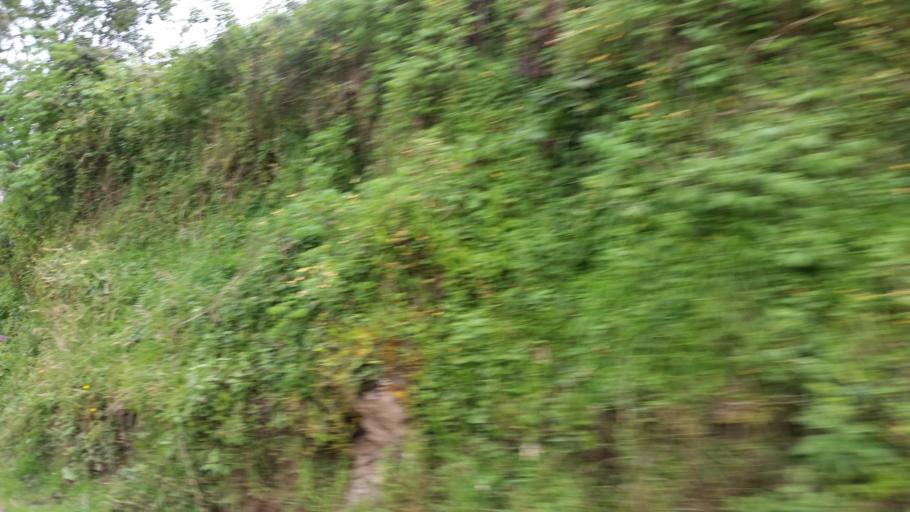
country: CO
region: Cundinamarca
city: Choachi
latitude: 4.5614
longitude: -73.9452
